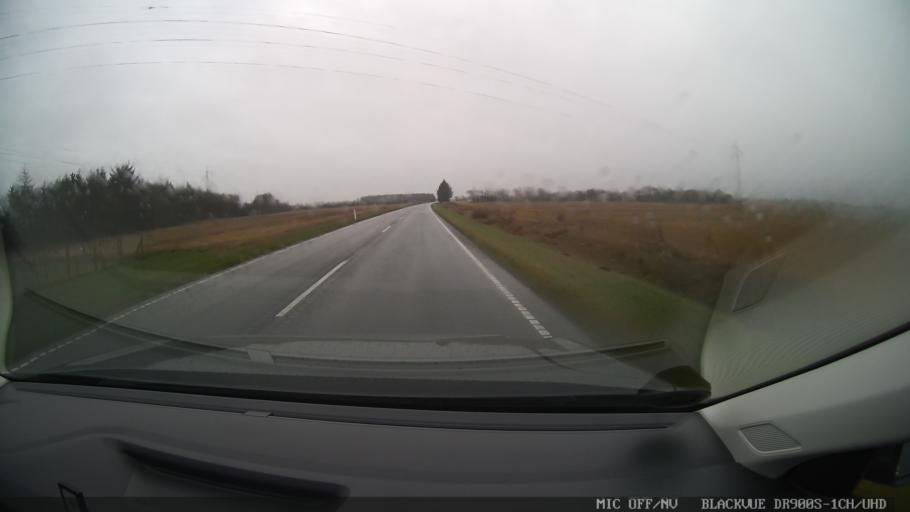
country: DK
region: Central Jutland
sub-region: Herning Kommune
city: Sunds
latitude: 56.2835
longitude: 8.9400
